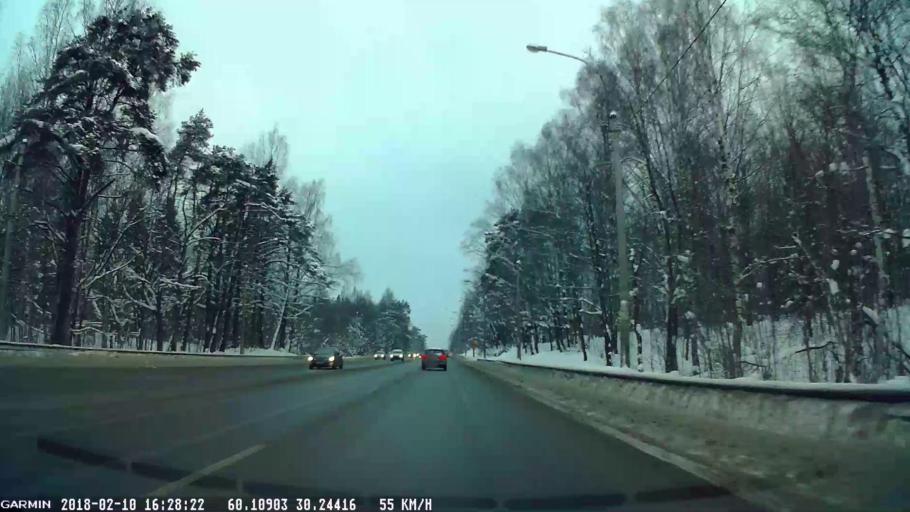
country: RU
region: St.-Petersburg
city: Levashovo
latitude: 60.1093
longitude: 30.2439
